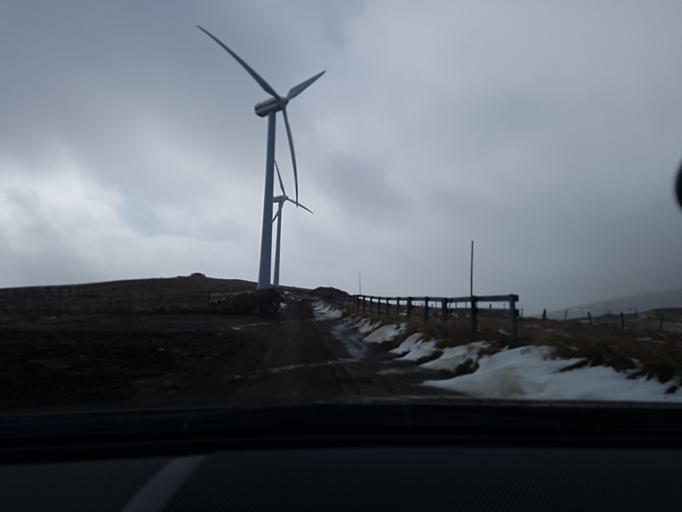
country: AT
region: Styria
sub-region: Politischer Bezirk Murtal
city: Pusterwald
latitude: 47.2690
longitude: 14.3792
